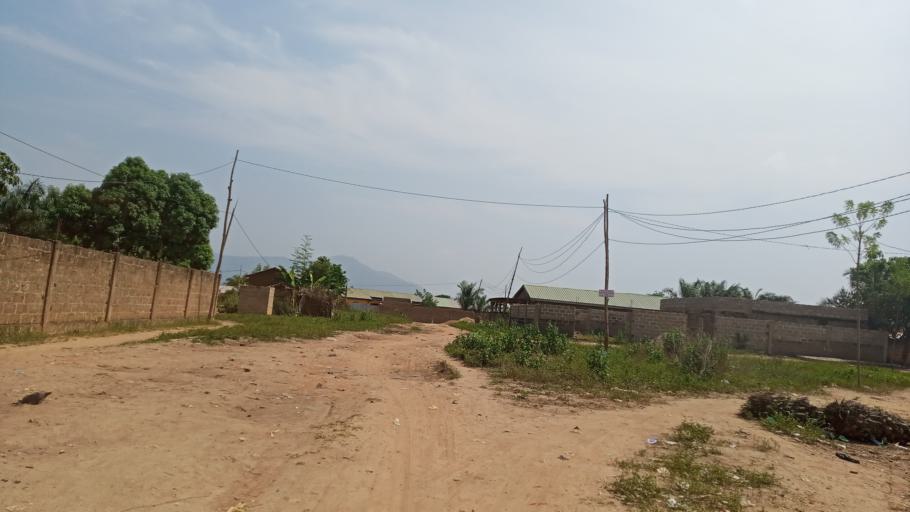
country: TG
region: Plateaux
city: Kpalime
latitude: 6.8969
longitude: 0.6501
